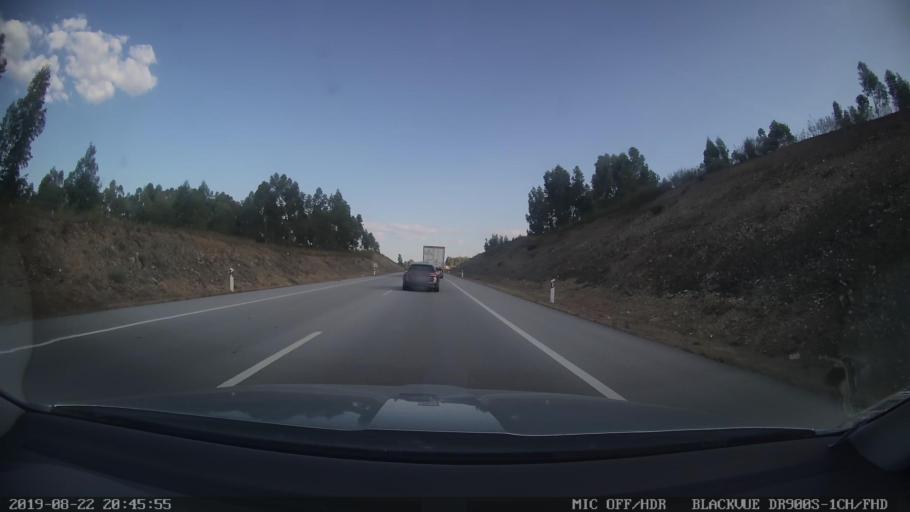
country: PT
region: Castelo Branco
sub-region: Proenca-A-Nova
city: Proenca-a-Nova
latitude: 39.7217
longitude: -7.8714
